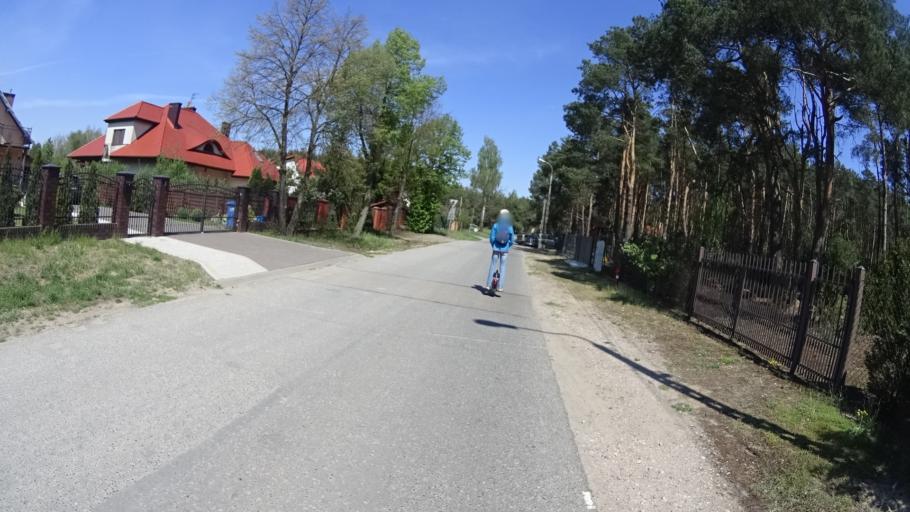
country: PL
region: Masovian Voivodeship
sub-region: Powiat warszawski zachodni
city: Truskaw
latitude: 52.2824
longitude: 20.7441
